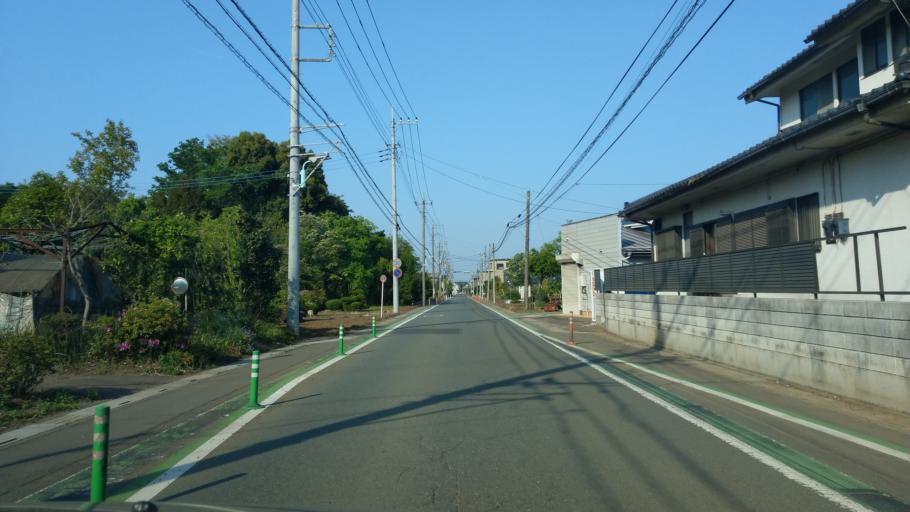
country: JP
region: Saitama
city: Tokorozawa
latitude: 35.8316
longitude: 139.4797
